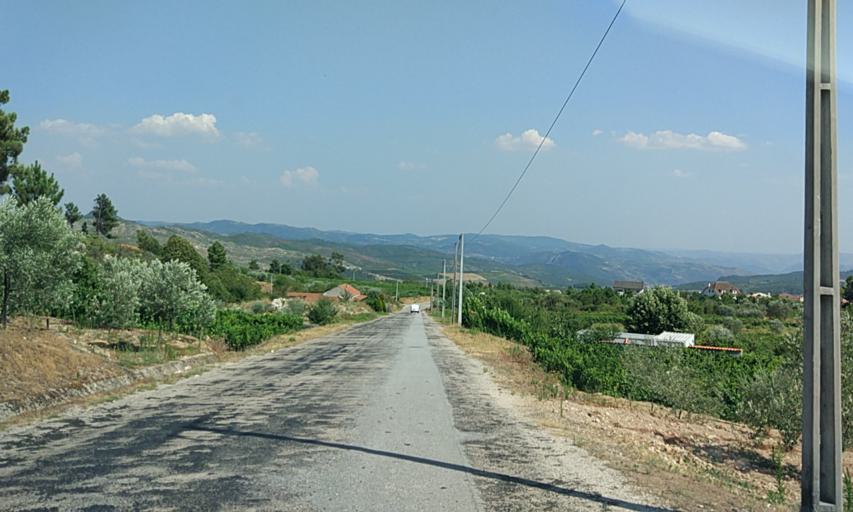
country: PT
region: Vila Real
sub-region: Sabrosa
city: Sabrosa
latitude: 41.2976
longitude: -7.4838
